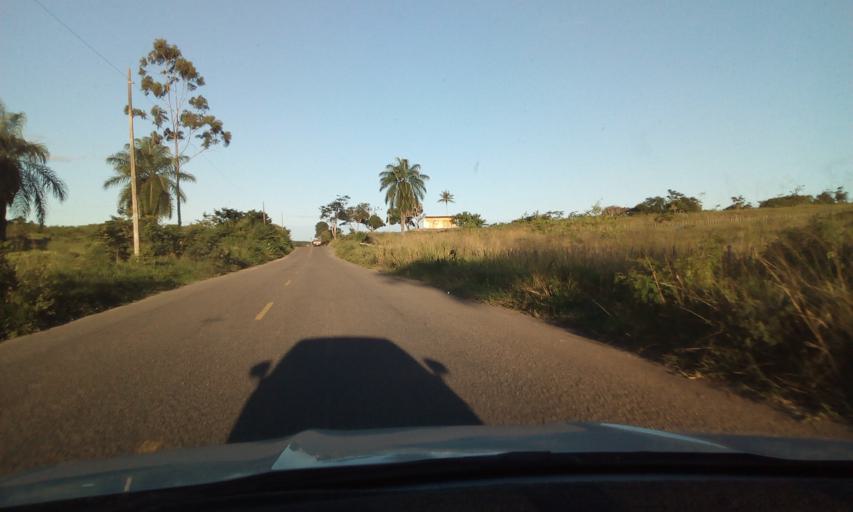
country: BR
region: Paraiba
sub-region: Areia
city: Remigio
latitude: -6.9615
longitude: -35.7751
